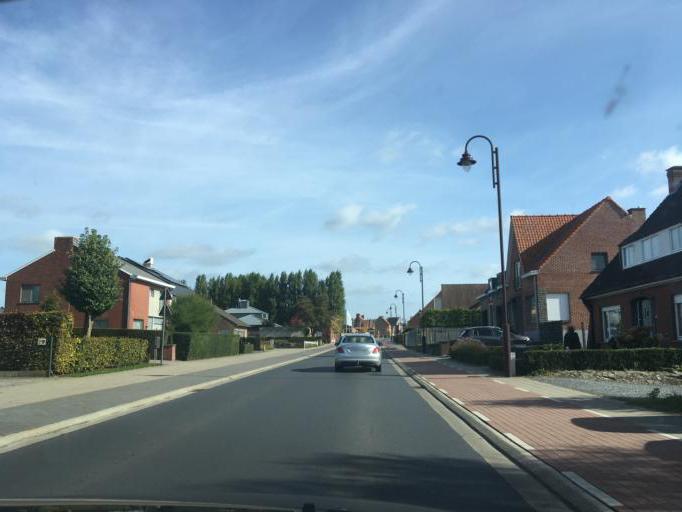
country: BE
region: Flanders
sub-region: Provincie West-Vlaanderen
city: Moorslede
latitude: 50.8883
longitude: 3.0559
